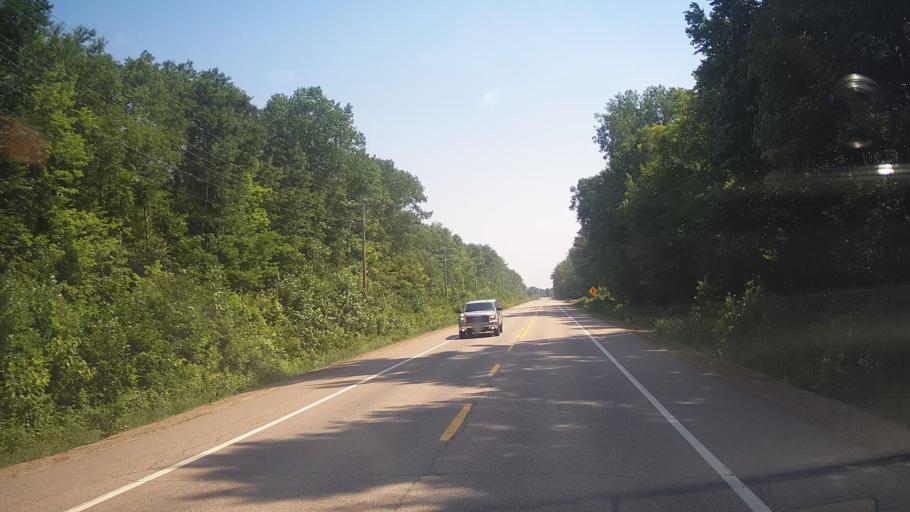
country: CA
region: Ontario
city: Pembroke
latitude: 45.8398
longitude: -77.0134
